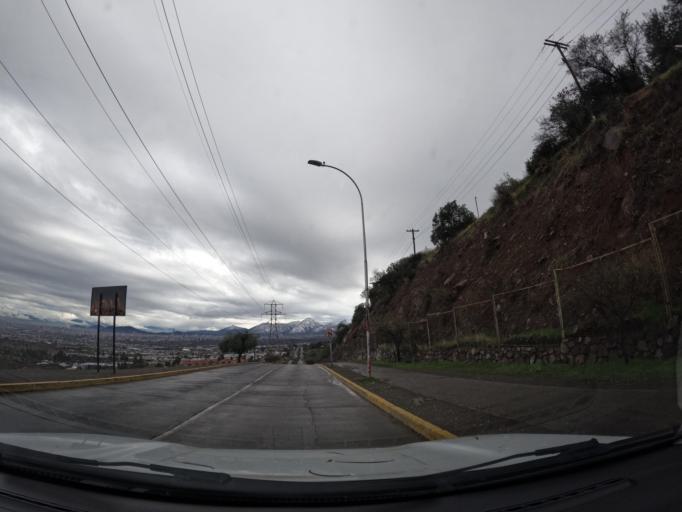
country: CL
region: Santiago Metropolitan
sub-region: Provincia de Santiago
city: Villa Presidente Frei, Nunoa, Santiago, Chile
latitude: -33.4887
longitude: -70.5198
